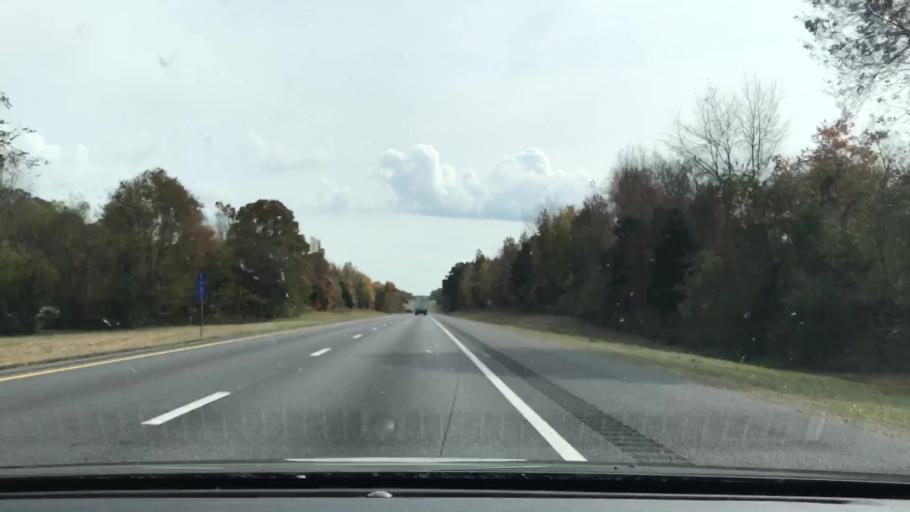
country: US
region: Tennessee
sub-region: Cheatham County
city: Pleasant View
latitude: 36.4850
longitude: -87.1571
